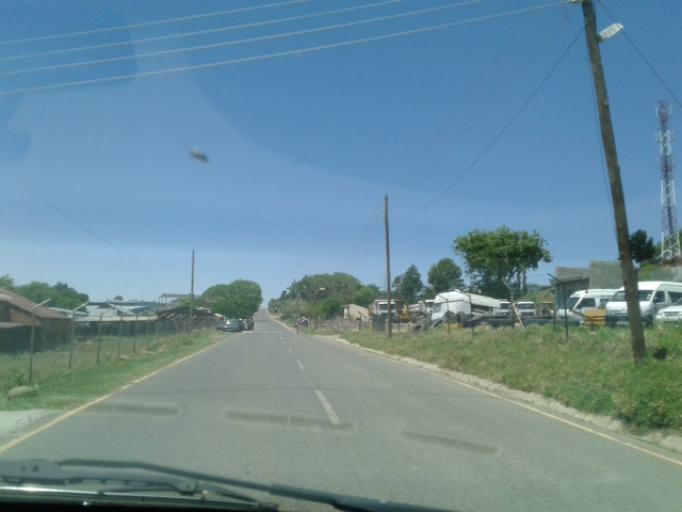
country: LS
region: Maseru
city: Maseru
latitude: -29.3006
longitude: 27.4750
